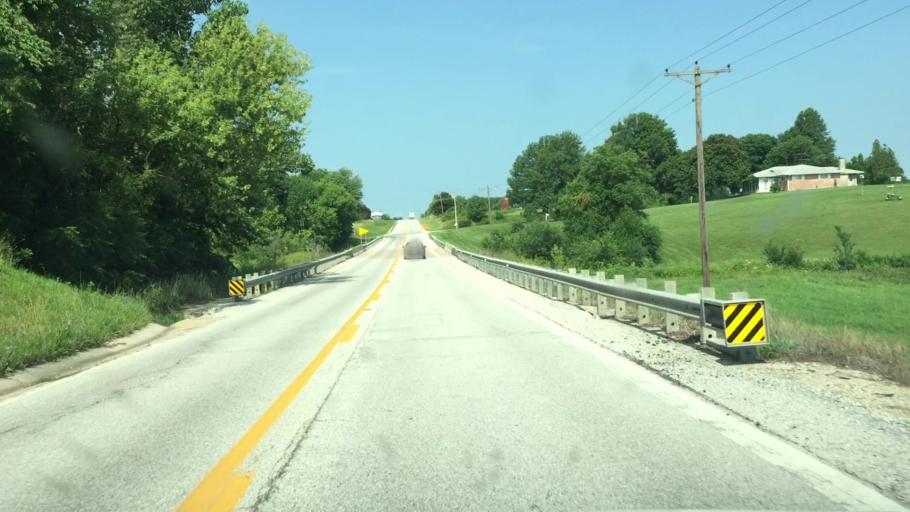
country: US
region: Illinois
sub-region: Hancock County
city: Nauvoo
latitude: 40.5517
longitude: -91.3246
